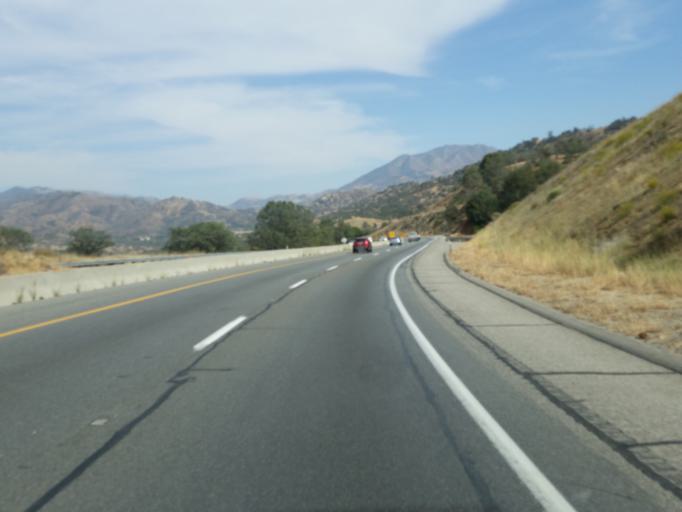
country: US
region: California
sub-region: Kern County
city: Bear Valley Springs
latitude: 35.2476
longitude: -118.5945
